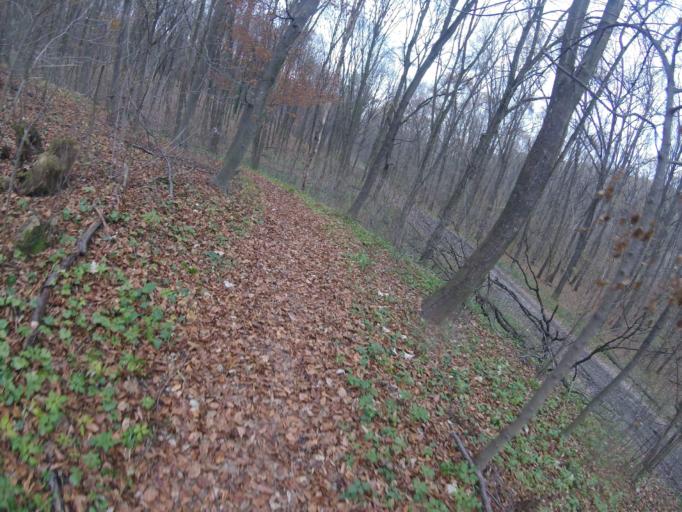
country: HU
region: Tolna
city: Szentgalpuszta
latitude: 46.3339
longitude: 18.6180
